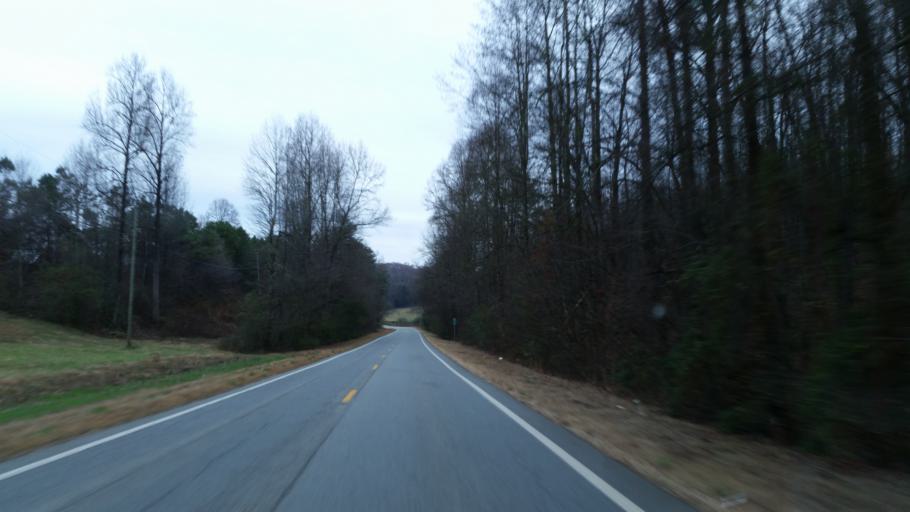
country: US
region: Georgia
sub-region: Dawson County
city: Dawsonville
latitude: 34.4760
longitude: -84.1565
